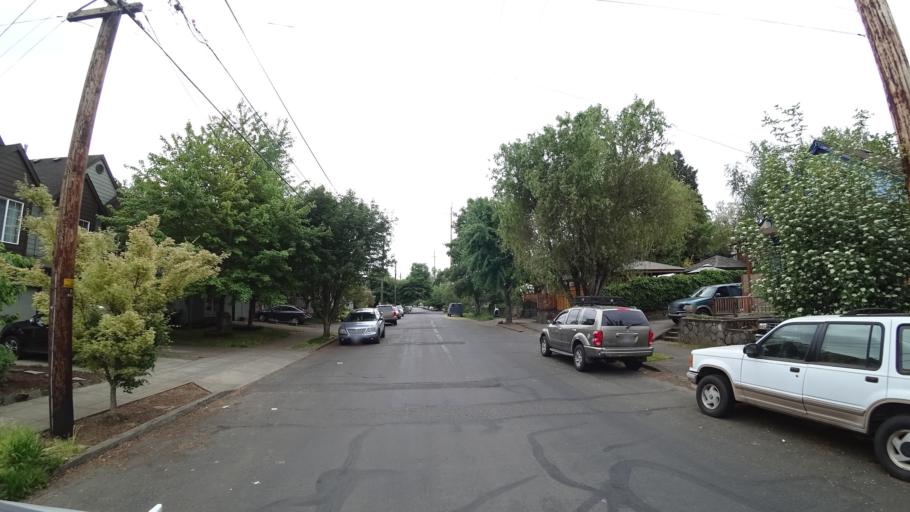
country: US
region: Oregon
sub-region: Multnomah County
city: Portland
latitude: 45.5542
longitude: -122.6637
